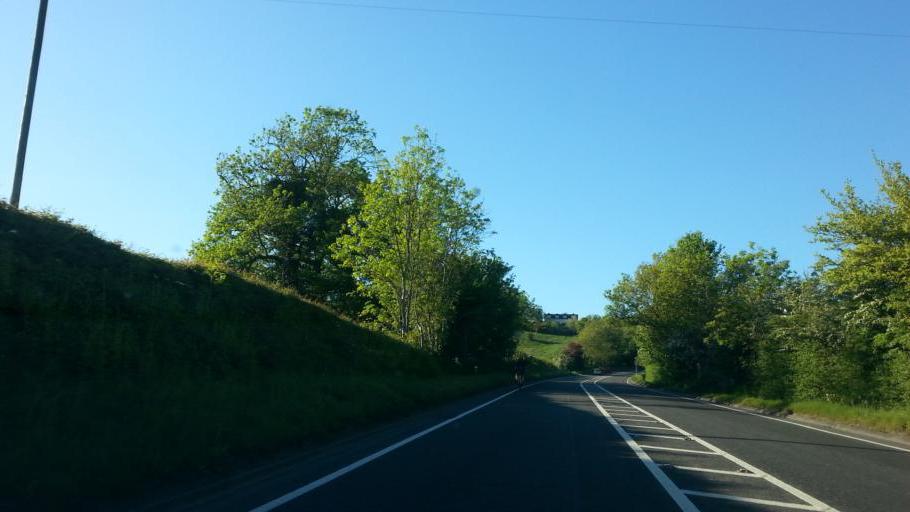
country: GB
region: England
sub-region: Bath and North East Somerset
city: Publow
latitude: 51.3886
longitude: -2.5509
